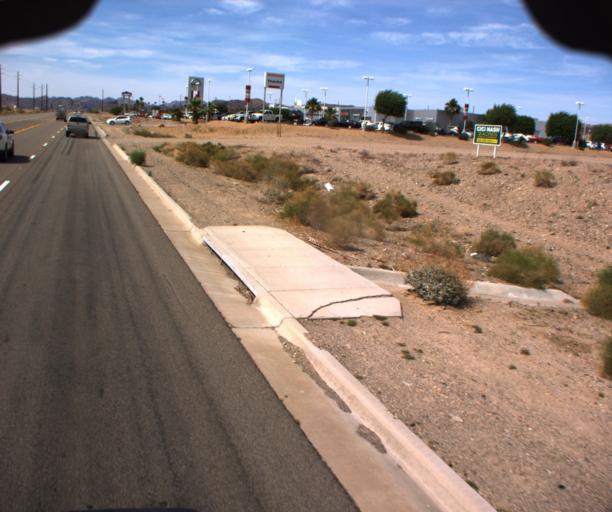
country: US
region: Arizona
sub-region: Mohave County
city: Desert Hills
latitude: 34.5409
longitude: -114.3531
